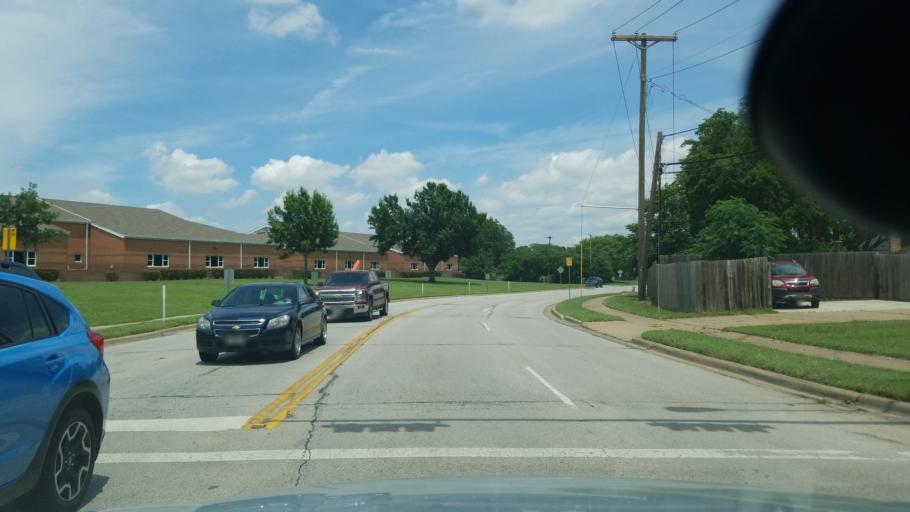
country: US
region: Texas
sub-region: Dallas County
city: Irving
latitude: 32.8441
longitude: -96.9661
